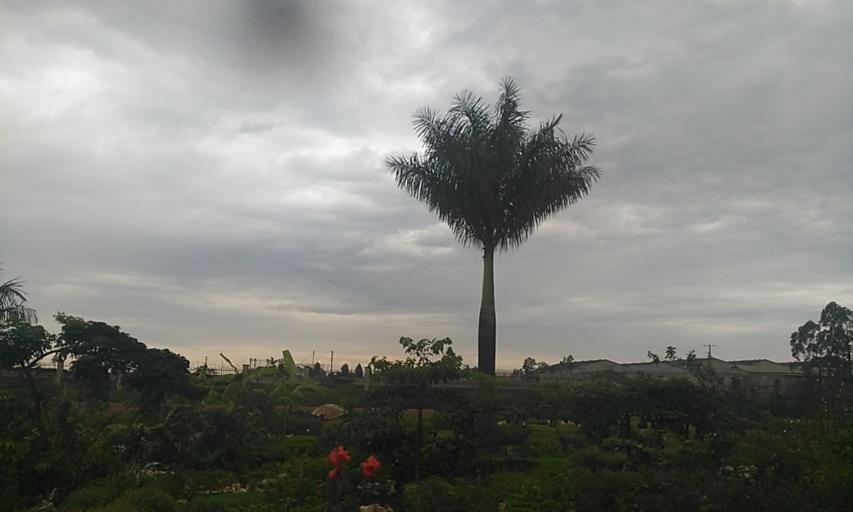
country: UG
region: Central Region
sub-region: Wakiso District
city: Bweyogerere
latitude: 0.3554
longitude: 32.6814
